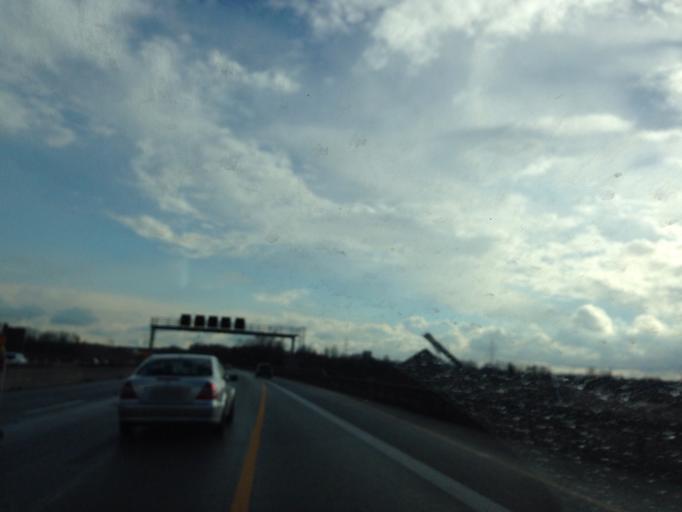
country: DE
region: North Rhine-Westphalia
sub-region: Regierungsbezirk Dusseldorf
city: Kaarst
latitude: 51.2469
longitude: 6.6380
